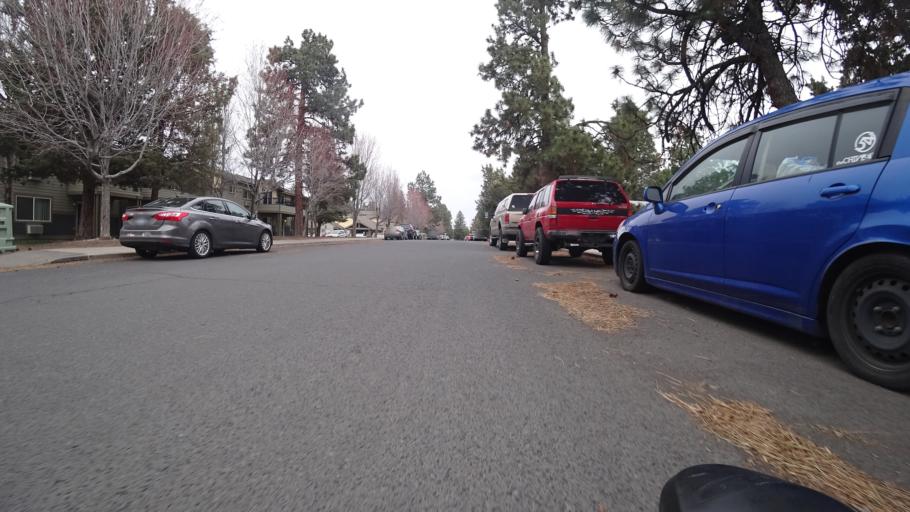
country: US
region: Oregon
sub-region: Deschutes County
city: Bend
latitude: 44.0460
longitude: -121.2813
